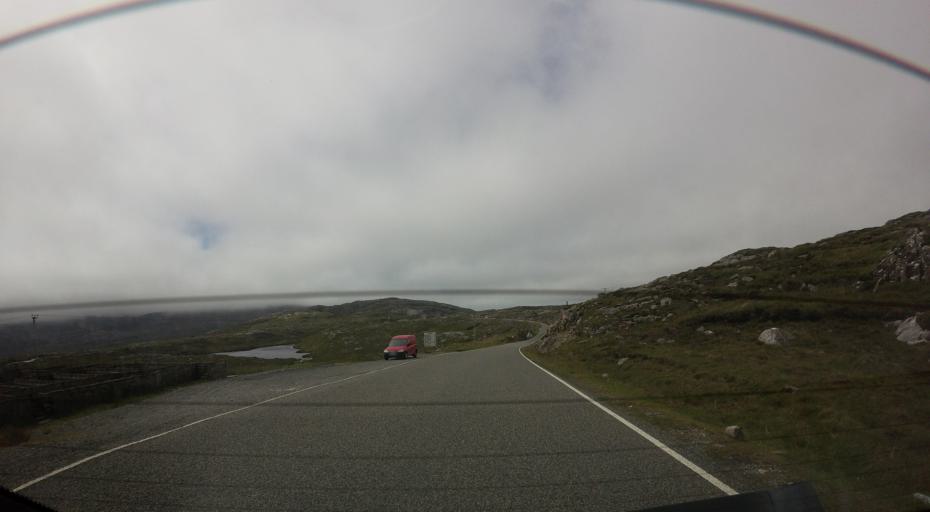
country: GB
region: Scotland
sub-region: Eilean Siar
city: Harris
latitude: 57.8469
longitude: -6.8314
